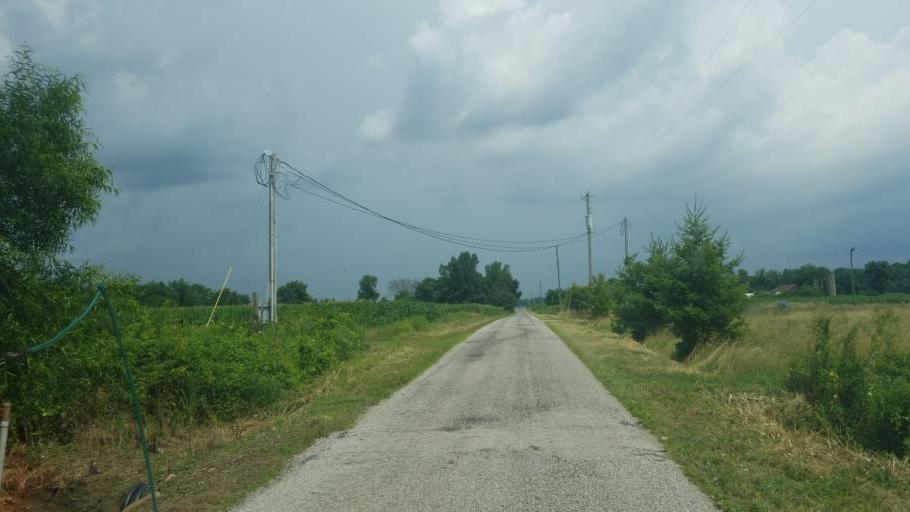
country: US
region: Ohio
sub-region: Wayne County
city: West Salem
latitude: 40.8324
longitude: -82.1429
